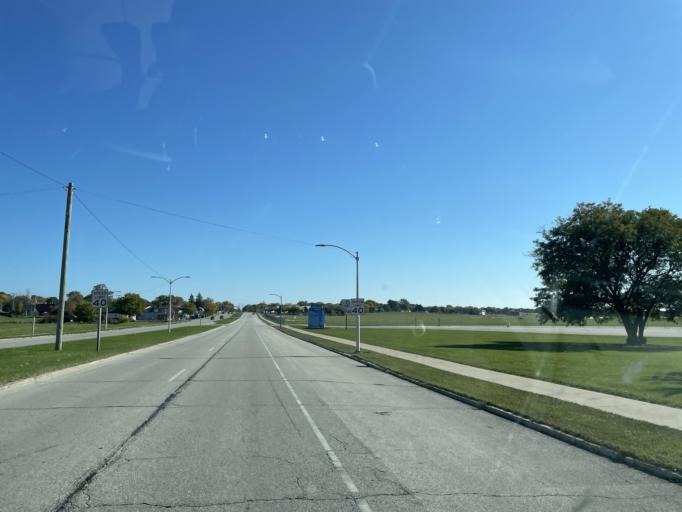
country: US
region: Wisconsin
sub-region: Waukesha County
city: Butler
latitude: 43.1165
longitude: -88.0310
